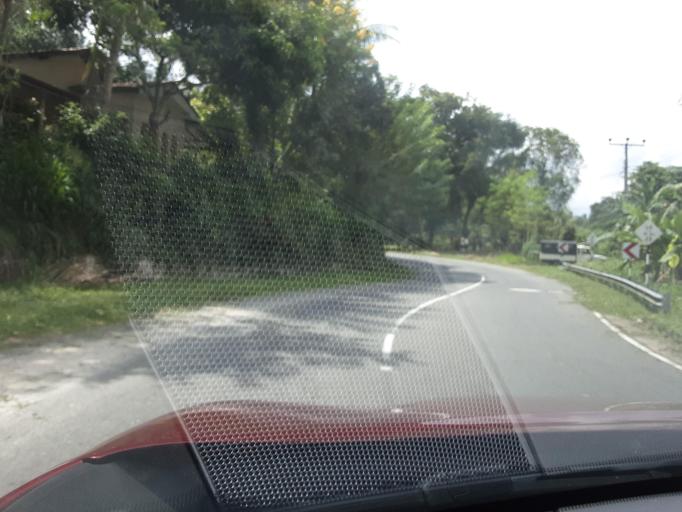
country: LK
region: Uva
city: Monaragala
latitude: 6.8965
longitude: 81.2742
